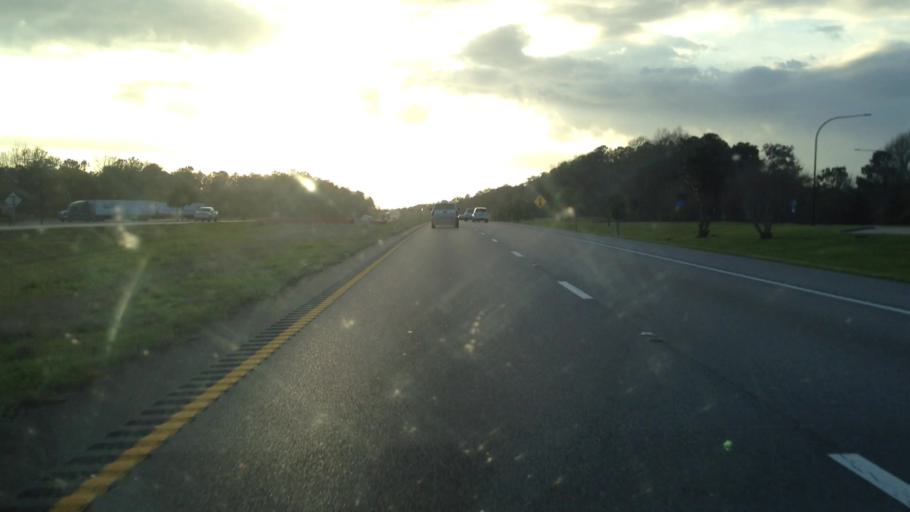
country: US
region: Mississippi
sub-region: Jackson County
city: Hickory Hills
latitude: 30.4382
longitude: -88.6200
